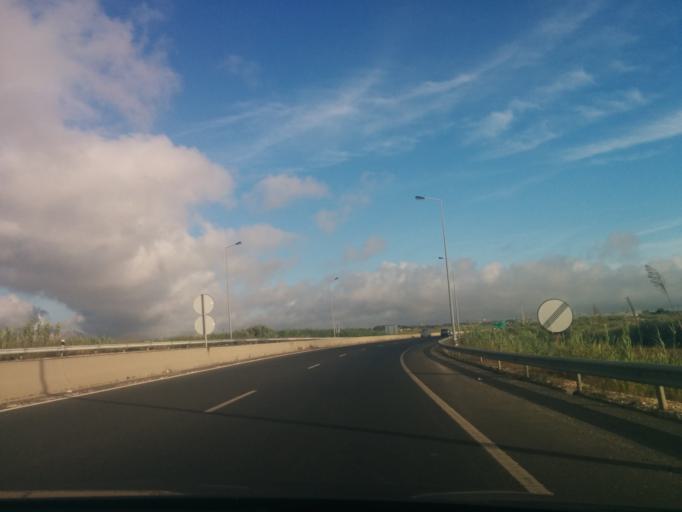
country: PT
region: Leiria
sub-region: Peniche
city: Atouguia da Baleia
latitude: 39.3449
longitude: -9.3410
